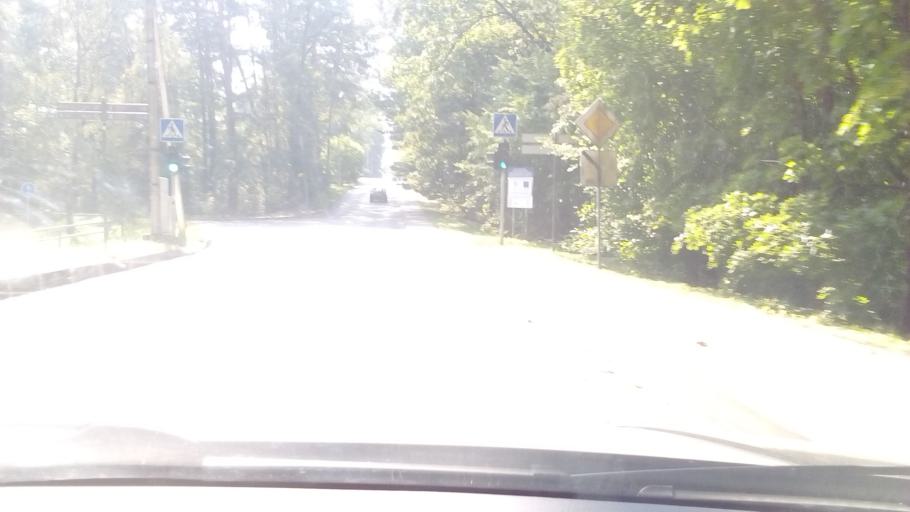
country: LT
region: Alytaus apskritis
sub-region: Alytus
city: Alytus
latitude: 54.3942
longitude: 24.0577
